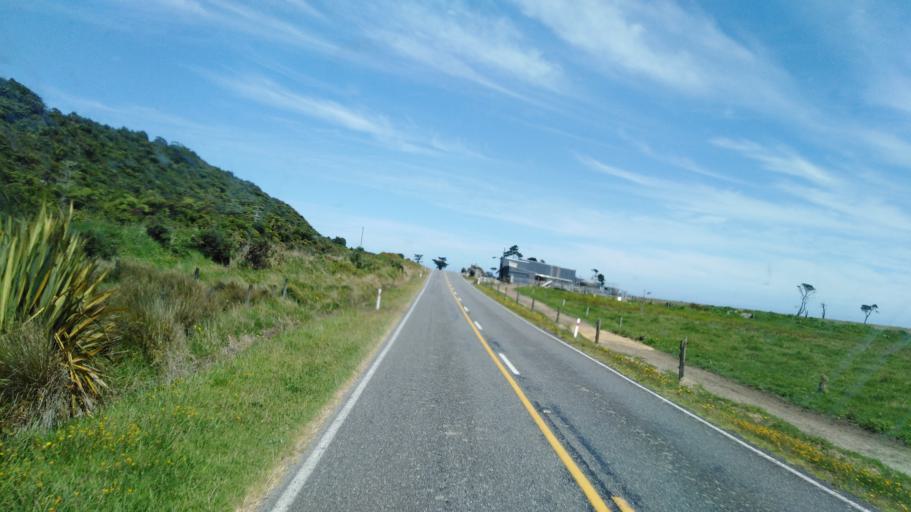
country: NZ
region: West Coast
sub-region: Buller District
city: Westport
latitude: -41.5329
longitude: 171.9378
